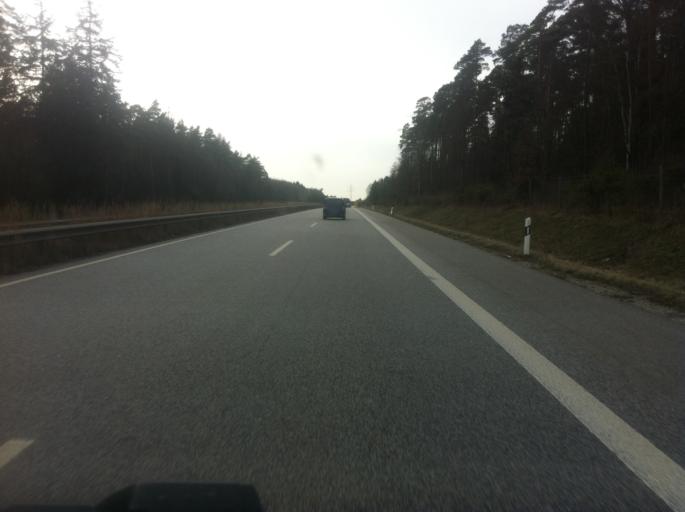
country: DE
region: Rheinland-Pfalz
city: Ober Kostenz
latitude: 49.9363
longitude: 7.3576
